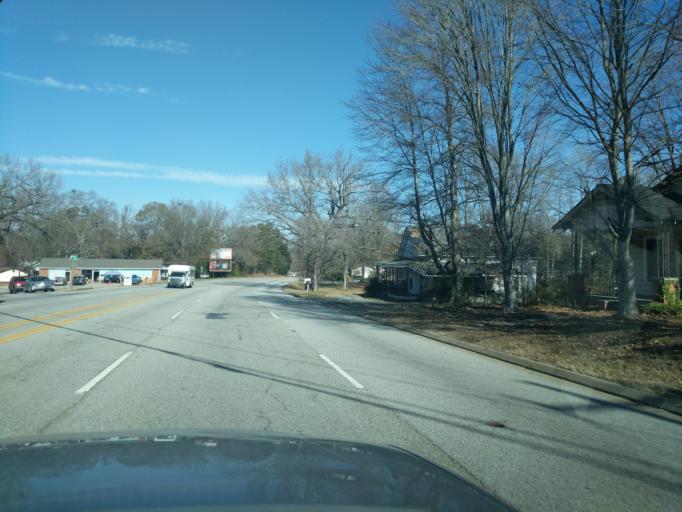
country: US
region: South Carolina
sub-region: Spartanburg County
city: Mayo
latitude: 35.0456
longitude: -81.8904
